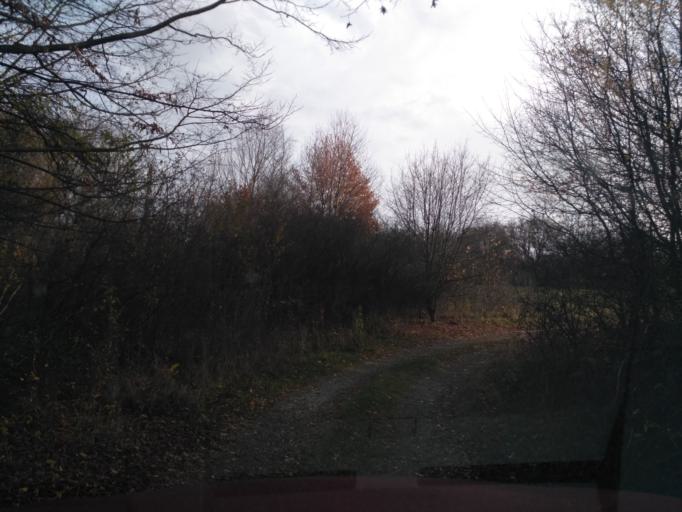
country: SK
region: Presovsky
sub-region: Okres Presov
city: Presov
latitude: 48.8742
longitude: 21.2282
